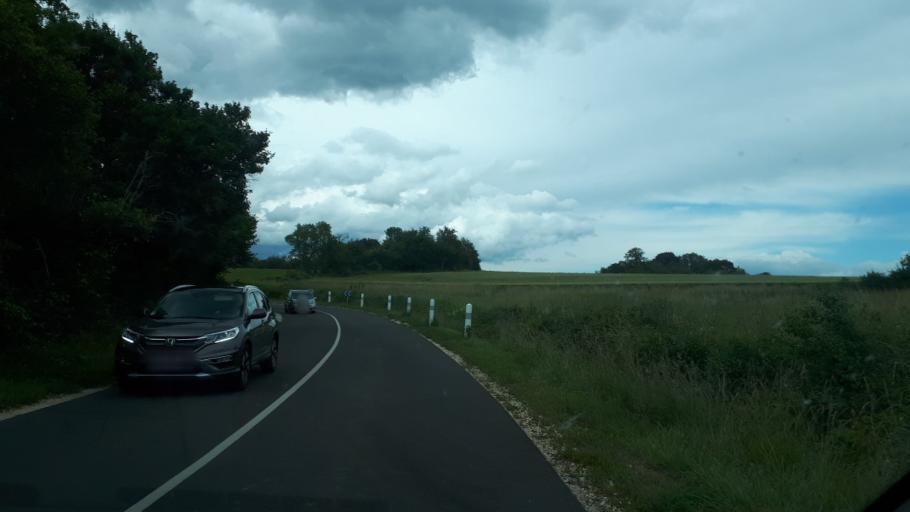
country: FR
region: Centre
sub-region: Departement du Cher
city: Gracay
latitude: 47.1575
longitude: 1.8380
